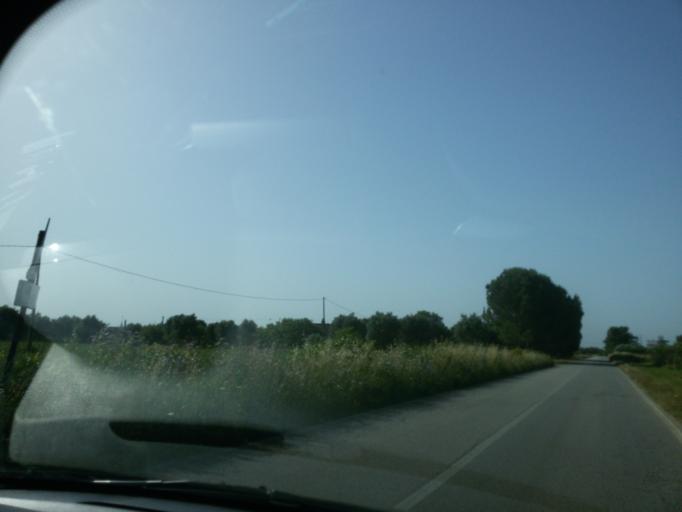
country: IT
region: Apulia
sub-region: Provincia di Brindisi
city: Mesagne
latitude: 40.5369
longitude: 17.8181
